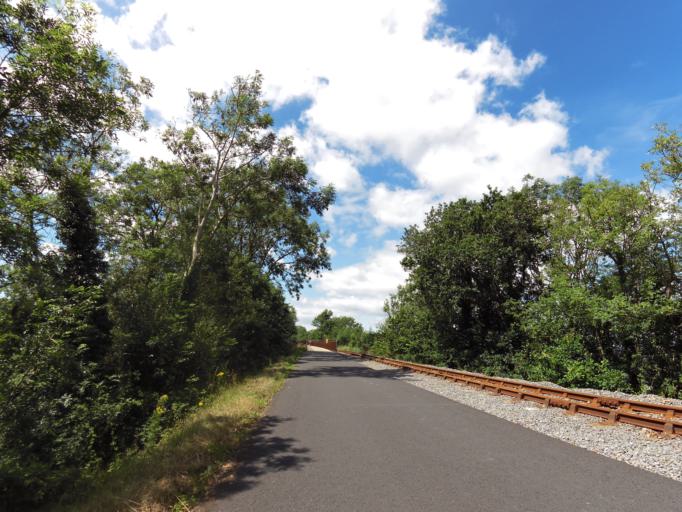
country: IE
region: Leinster
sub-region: Kilkenny
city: Mooncoin
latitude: 52.2459
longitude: -7.2294
